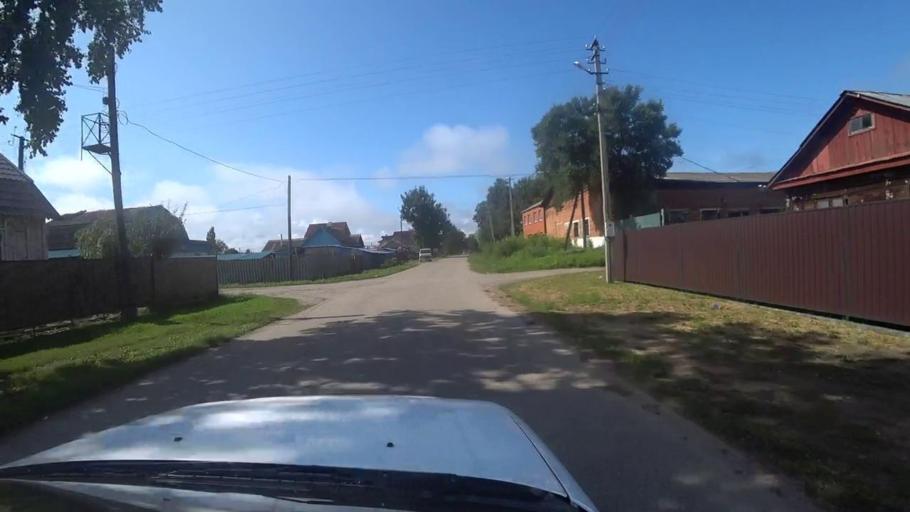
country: RU
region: Primorskiy
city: Dal'nerechensk
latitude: 45.9273
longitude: 133.7238
